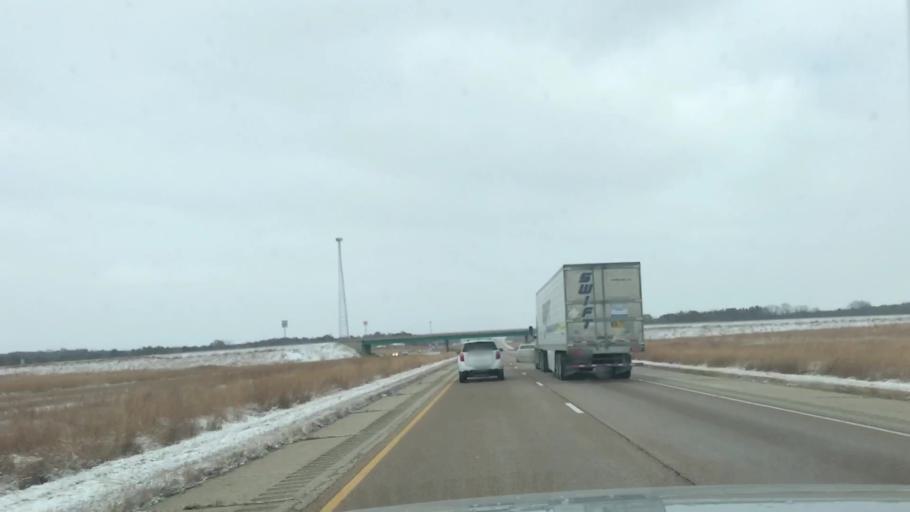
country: US
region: Illinois
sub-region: Montgomery County
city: Raymond
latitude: 39.2753
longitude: -89.6416
